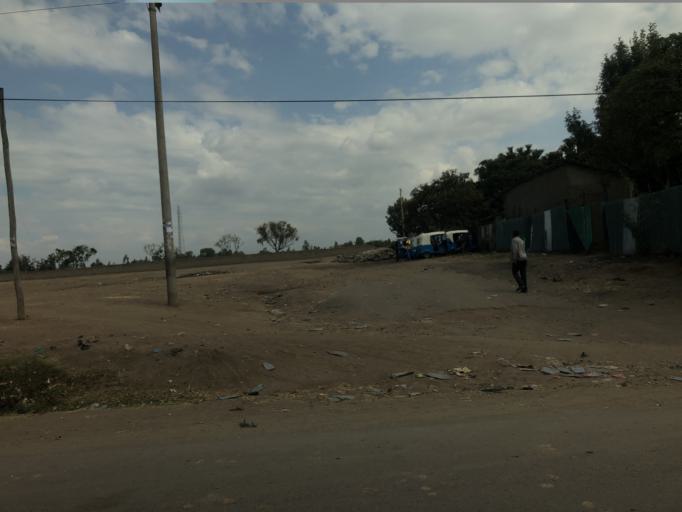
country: ET
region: Oromiya
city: Shashemene
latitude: 7.3631
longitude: 38.6712
